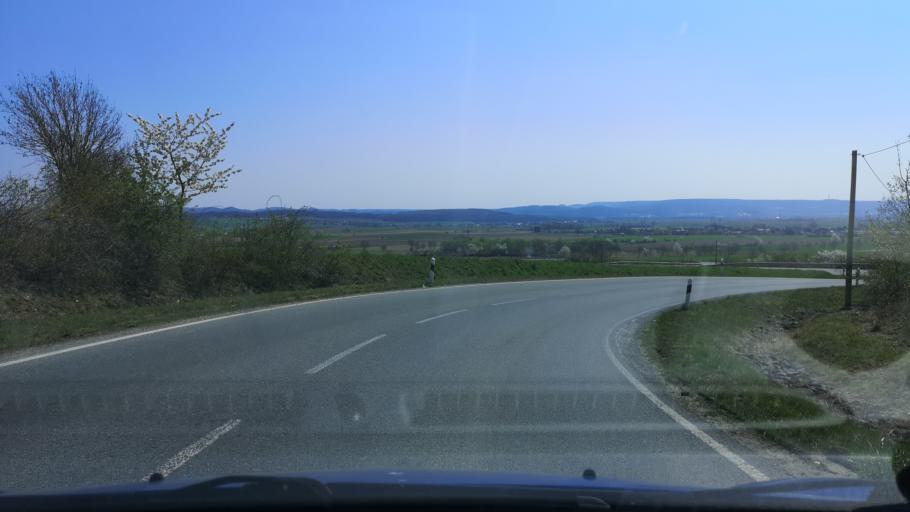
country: DE
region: Lower Saxony
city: Moringen
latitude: 51.6807
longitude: 9.8488
